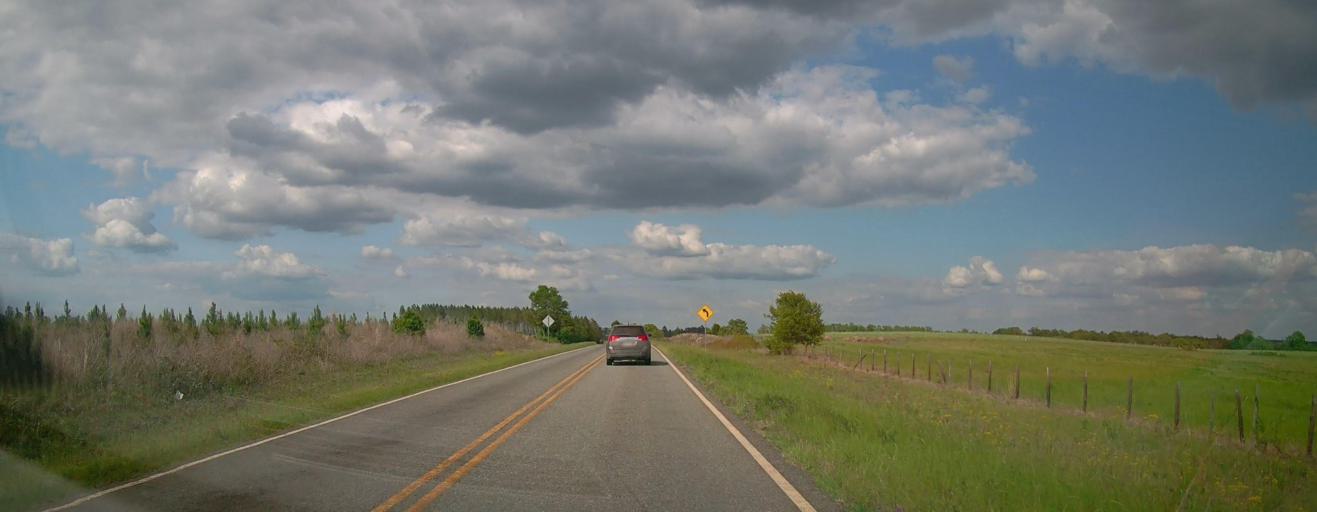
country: US
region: Georgia
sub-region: Laurens County
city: East Dublin
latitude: 32.7222
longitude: -82.9144
